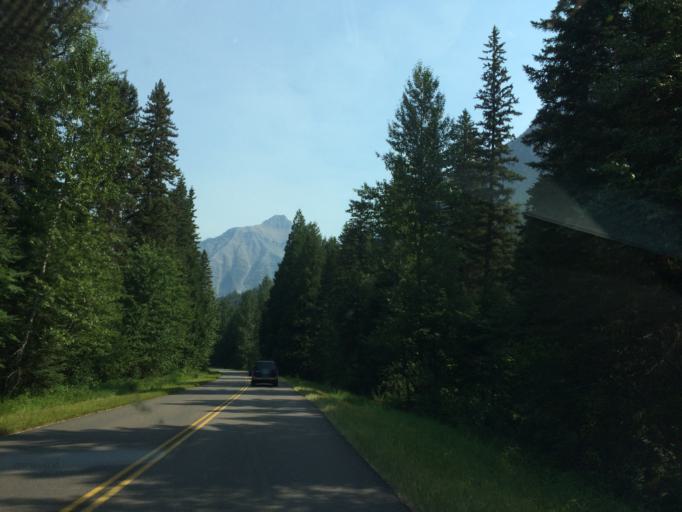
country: US
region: Montana
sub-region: Flathead County
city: Columbia Falls
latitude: 48.6469
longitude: -113.8447
